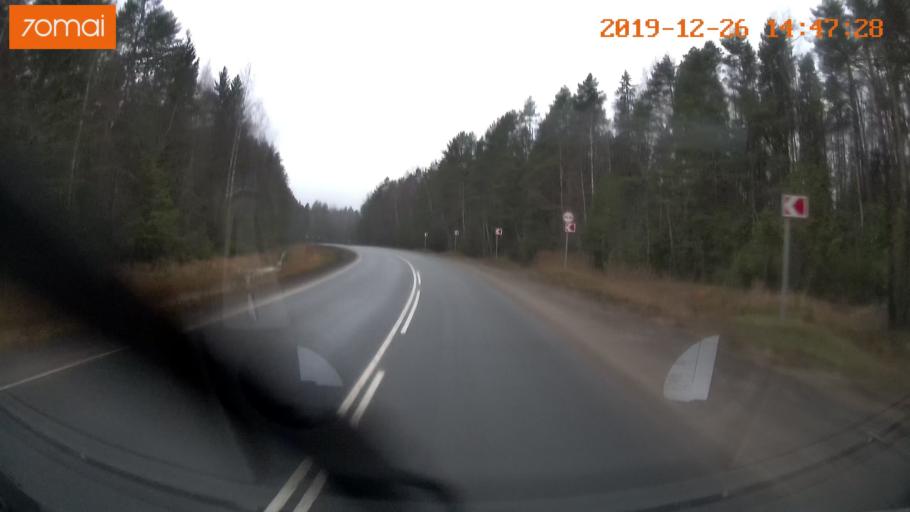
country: RU
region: Jaroslavl
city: Poshekhon'ye
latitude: 58.3423
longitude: 38.9972
